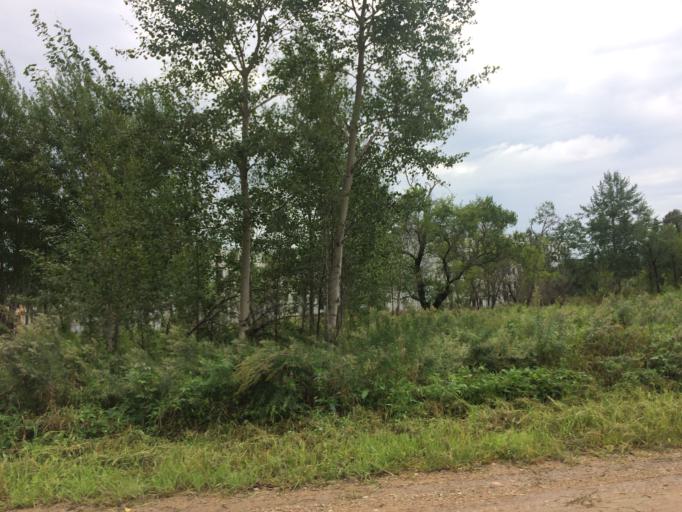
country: RU
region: Primorskiy
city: Lazo
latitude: 45.8241
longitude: 133.6412
